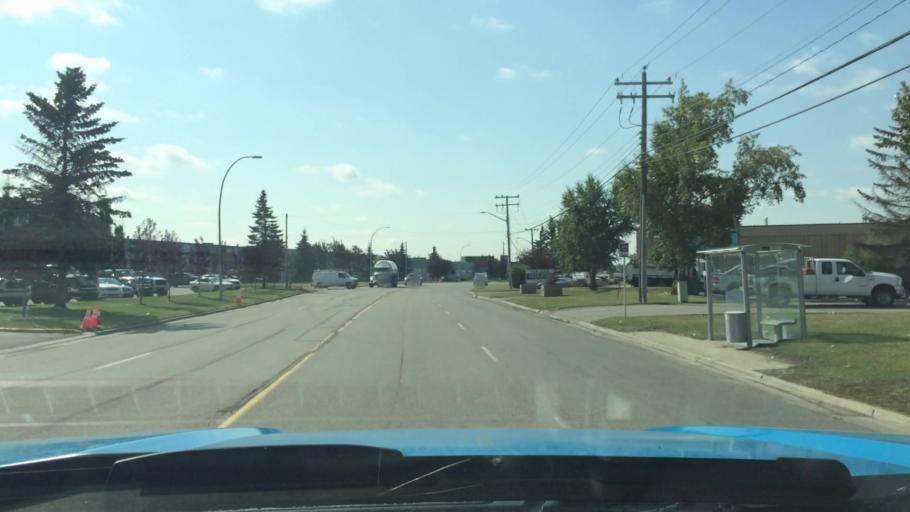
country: CA
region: Alberta
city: Calgary
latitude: 51.0852
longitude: -114.0302
